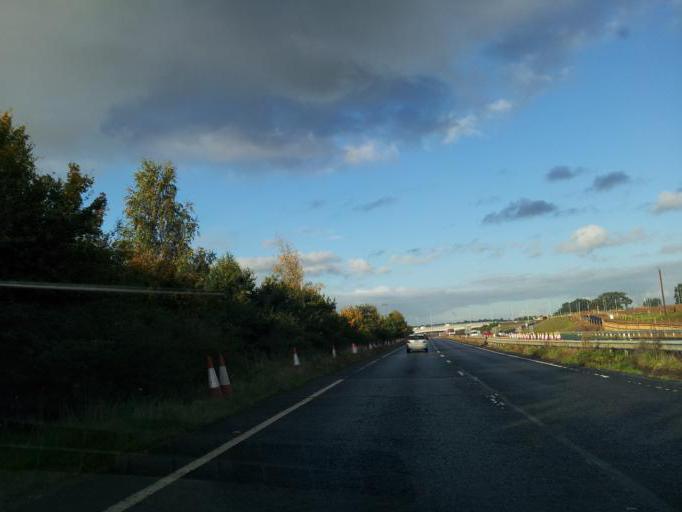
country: GB
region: England
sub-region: Norfolk
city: Surlingham
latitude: 52.6258
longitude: 1.3898
